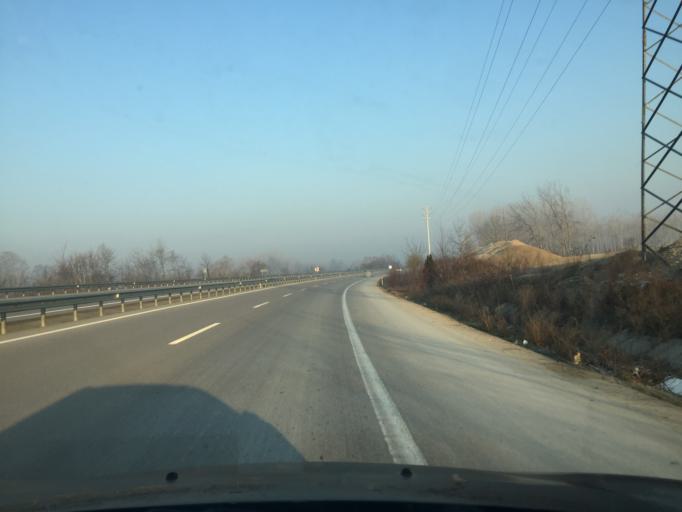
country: TR
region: Sakarya
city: Akyazi
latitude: 40.6803
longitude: 30.5782
